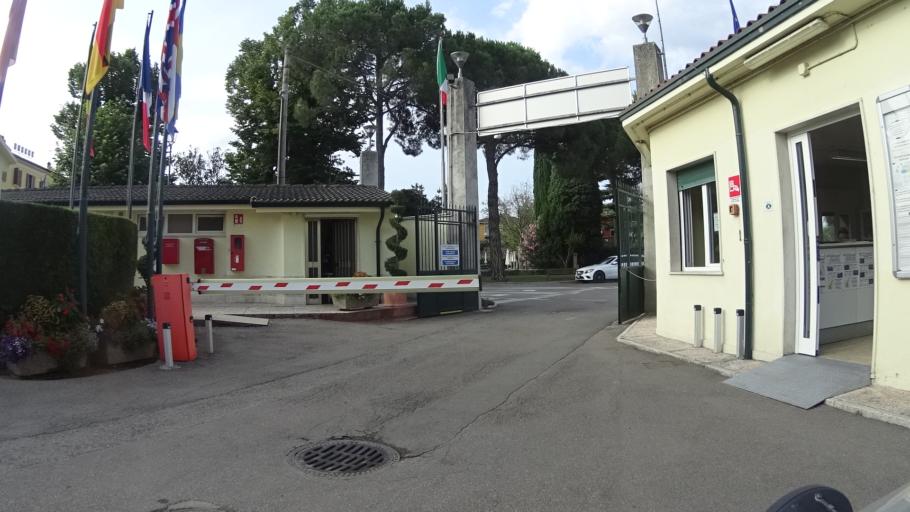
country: IT
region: Veneto
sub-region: Provincia di Verona
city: Lazise
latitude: 45.5083
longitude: 10.7318
